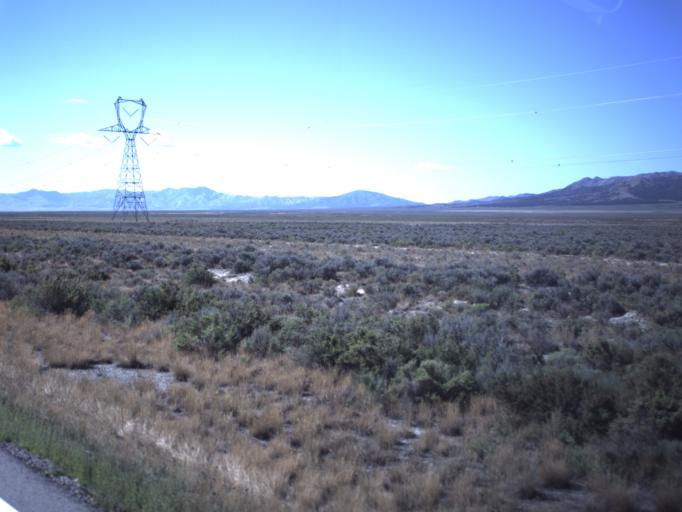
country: US
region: Utah
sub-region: Tooele County
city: Tooele
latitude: 40.2860
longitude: -112.3998
